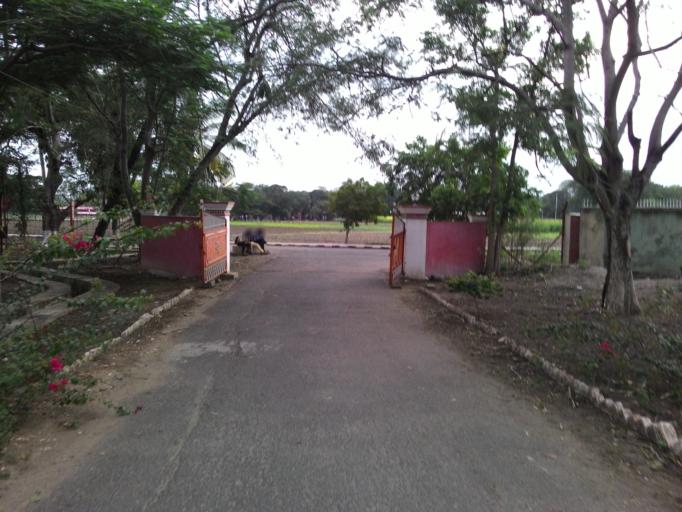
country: IN
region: Tamil Nadu
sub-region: Coimbatore
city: Coimbatore
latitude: 11.0092
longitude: 76.9395
